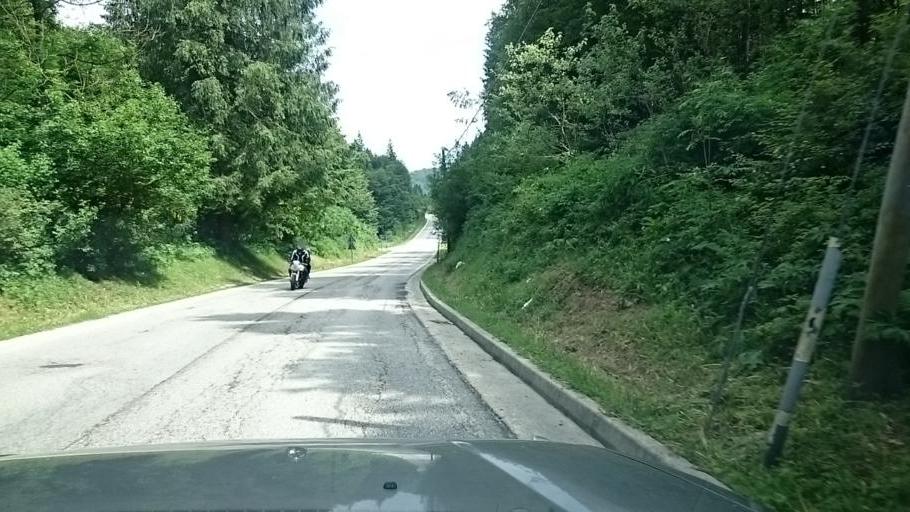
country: IT
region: Veneto
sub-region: Provincia di Vicenza
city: Conco
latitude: 45.8267
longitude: 11.5998
